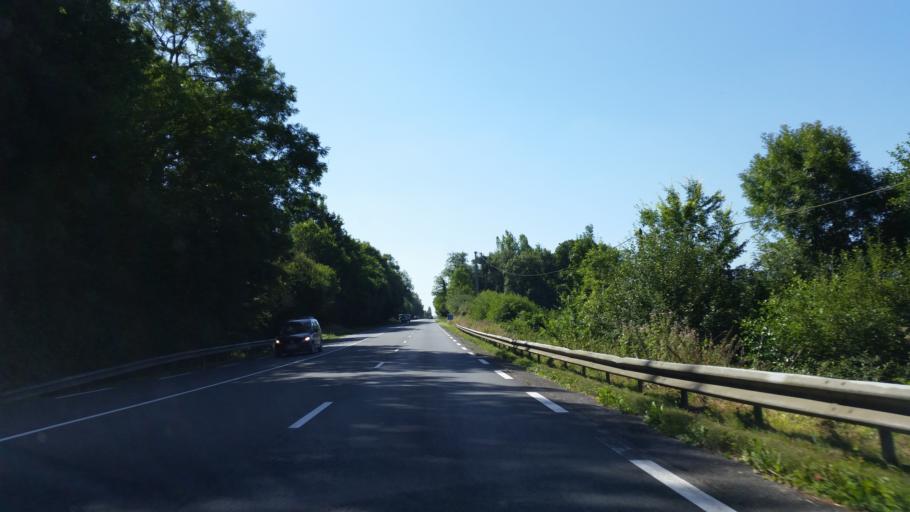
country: FR
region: Lower Normandy
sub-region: Departement du Calvados
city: Lisieux
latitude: 49.2438
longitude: 0.2215
